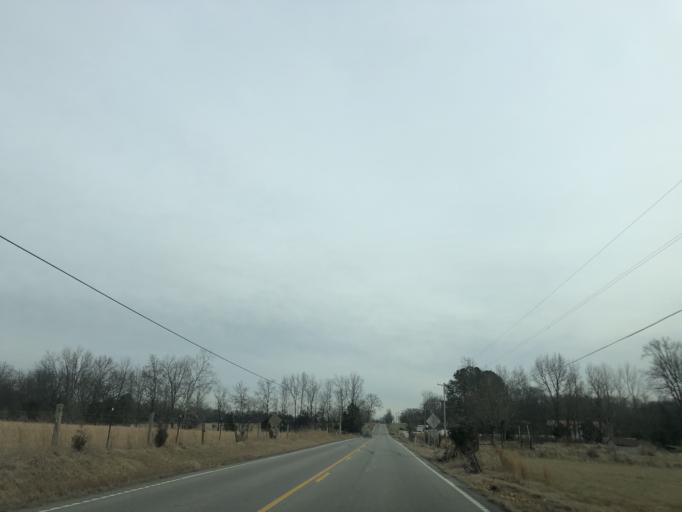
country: US
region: Tennessee
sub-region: Sumner County
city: White House
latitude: 36.5004
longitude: -86.6052
